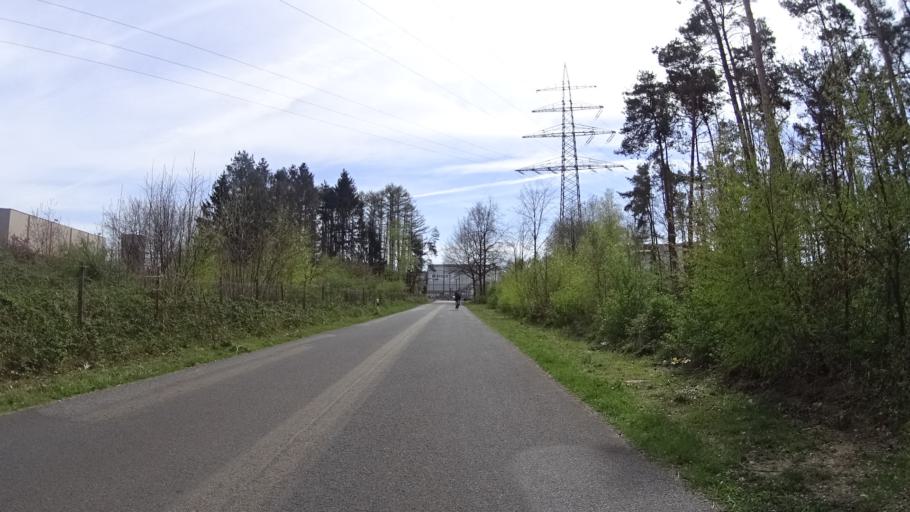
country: DE
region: Lower Saxony
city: Lingen
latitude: 52.4709
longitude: 7.3156
